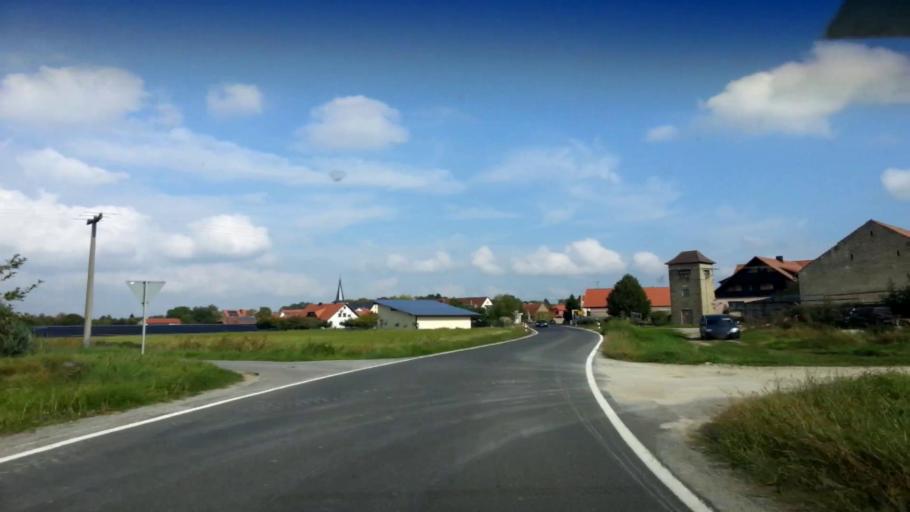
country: DE
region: Bavaria
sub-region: Regierungsbezirk Unterfranken
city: Prichsenstadt
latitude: 49.8108
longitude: 10.3838
